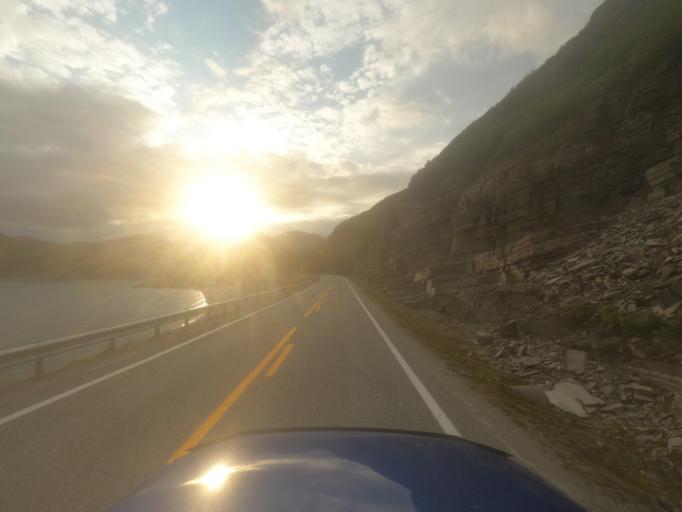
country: NO
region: Finnmark Fylke
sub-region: Nordkapp
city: Honningsvag
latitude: 70.6716
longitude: 25.4260
